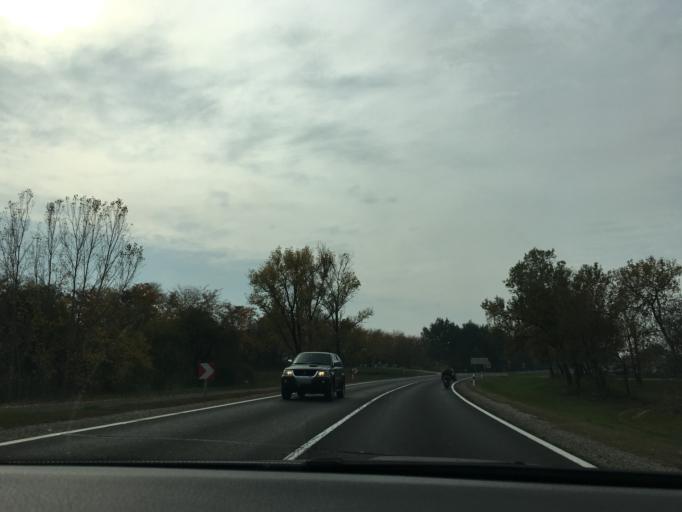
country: HU
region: Hajdu-Bihar
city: Debrecen
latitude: 47.5058
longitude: 21.5927
